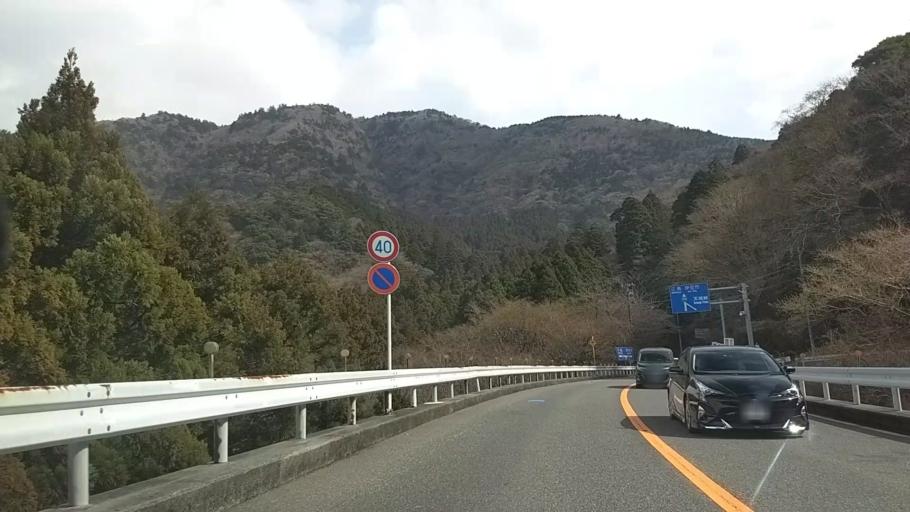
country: JP
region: Shizuoka
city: Shimoda
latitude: 34.8143
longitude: 138.9296
